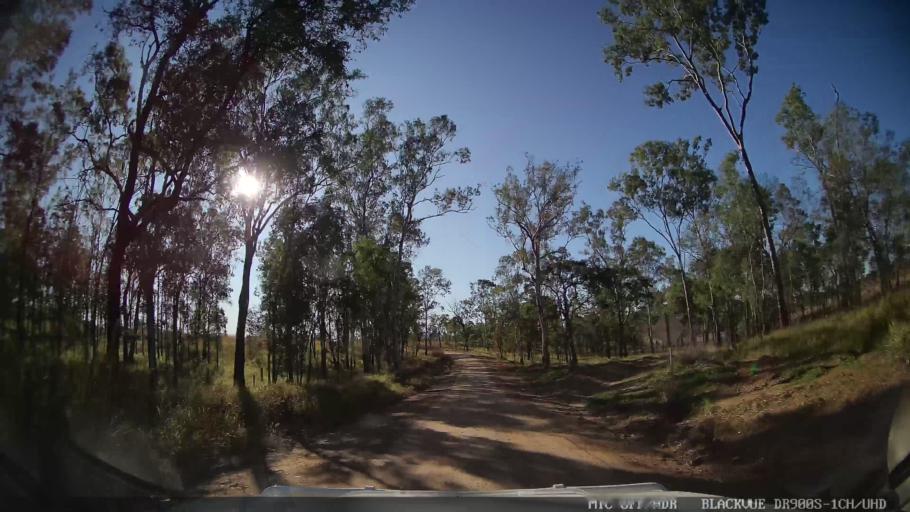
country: AU
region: Queensland
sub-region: Bundaberg
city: Sharon
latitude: -24.7886
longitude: 151.6073
